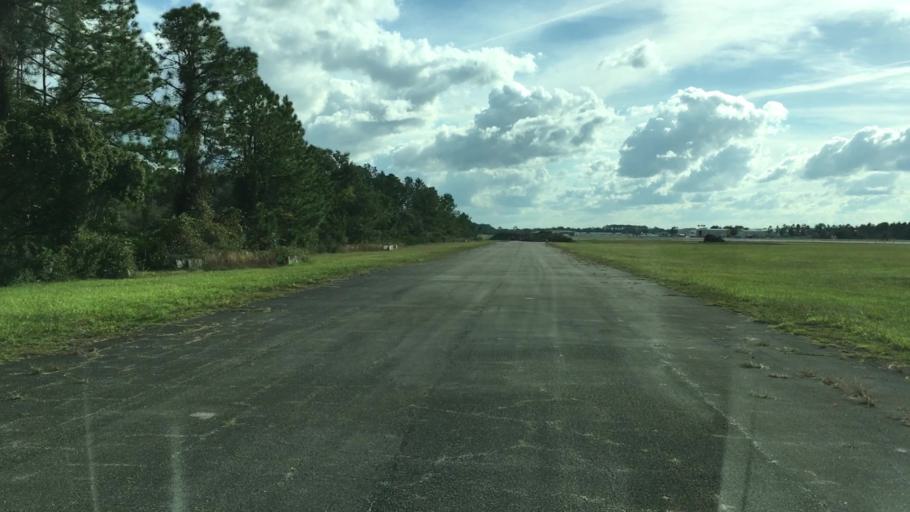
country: US
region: Florida
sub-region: Volusia County
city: North DeLand
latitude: 29.0743
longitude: -81.2853
